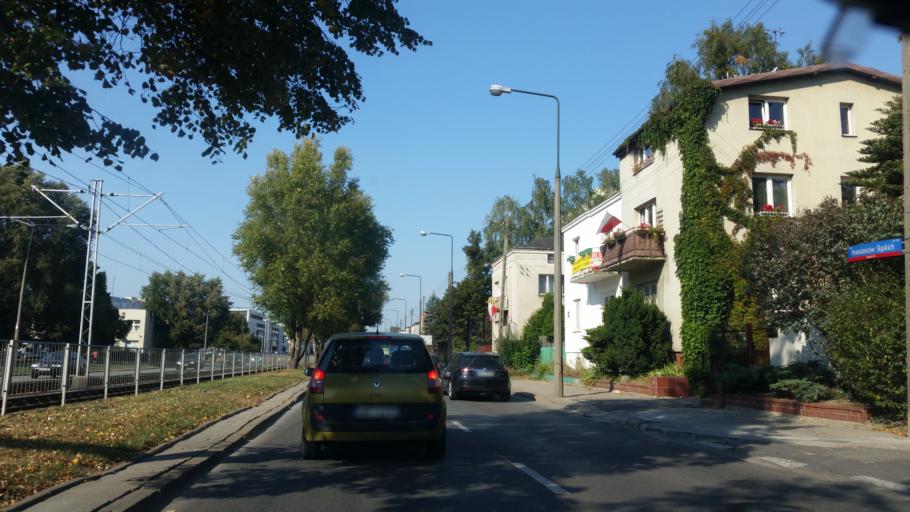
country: PL
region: Masovian Voivodeship
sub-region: Warszawa
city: Bemowo
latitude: 52.2266
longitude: 20.9162
